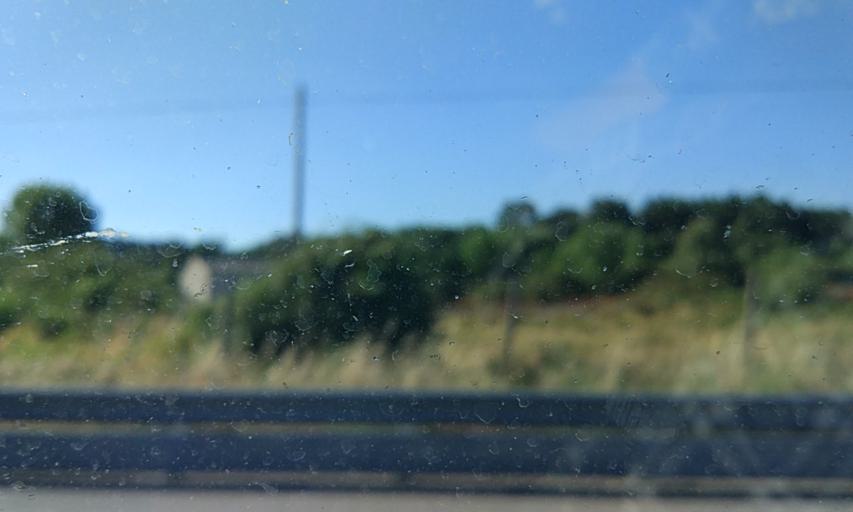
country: PT
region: Vila Real
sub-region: Sabrosa
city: Sabrosa
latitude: 41.3401
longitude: -7.6140
